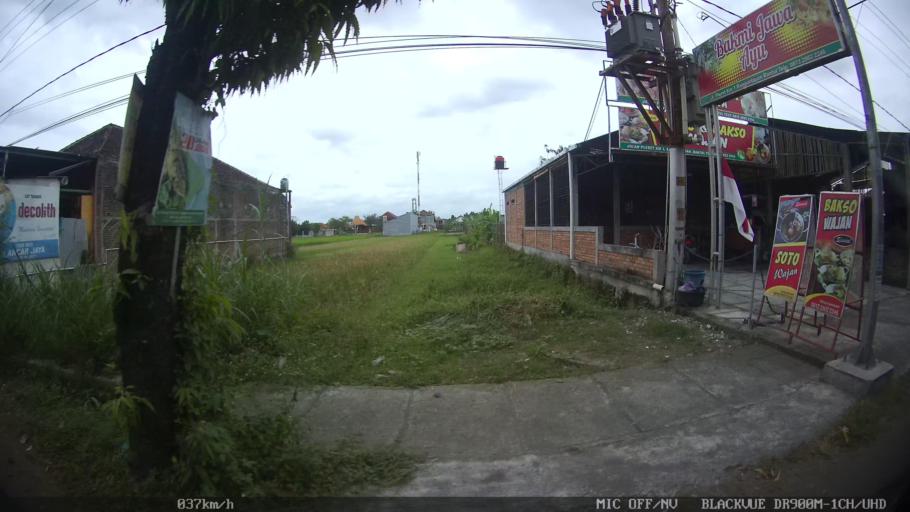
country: ID
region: Daerah Istimewa Yogyakarta
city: Sewon
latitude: -7.8312
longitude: 110.4127
